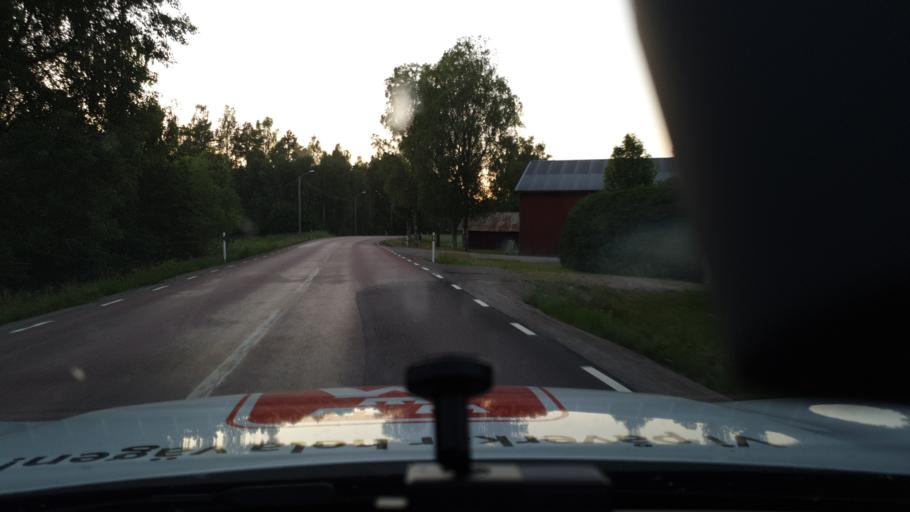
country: SE
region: Vaermland
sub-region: Torsby Kommun
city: Torsby
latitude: 60.2790
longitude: 13.0328
